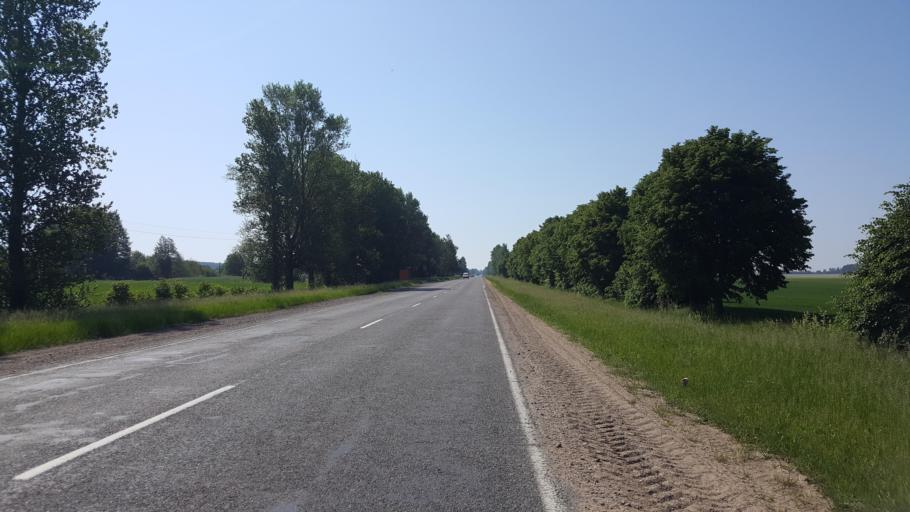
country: BY
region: Brest
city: Kamyanyets
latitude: 52.3597
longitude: 23.8924
